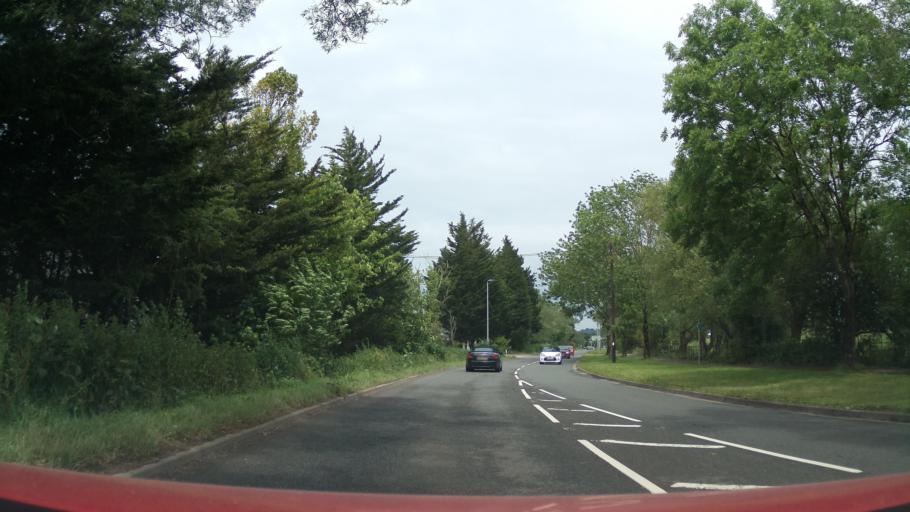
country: GB
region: Wales
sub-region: Vale of Glamorgan
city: Dinas Powys
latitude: 51.4088
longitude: -3.2280
